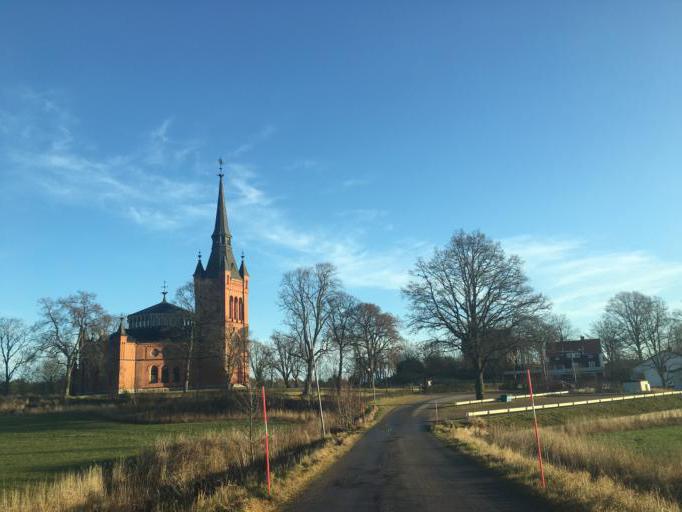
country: SE
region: Kalmar
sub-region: Vasterviks Kommun
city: Ankarsrum
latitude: 57.7091
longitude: 16.4507
